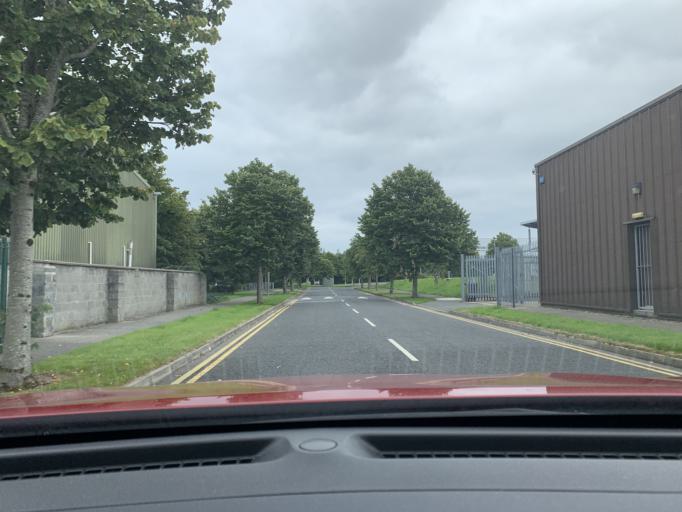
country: IE
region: Connaught
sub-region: Sligo
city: Sligo
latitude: 54.2748
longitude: -8.4953
